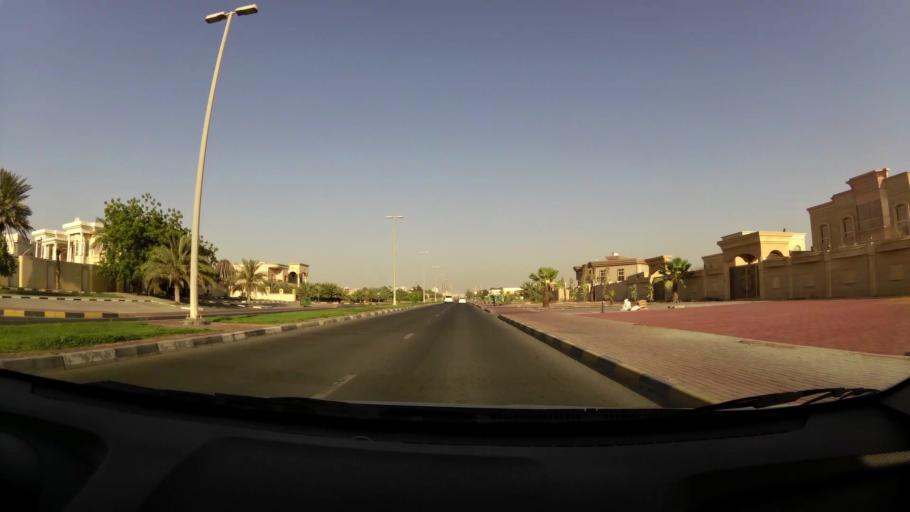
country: AE
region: Ajman
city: Ajman
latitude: 25.4085
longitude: 55.4867
